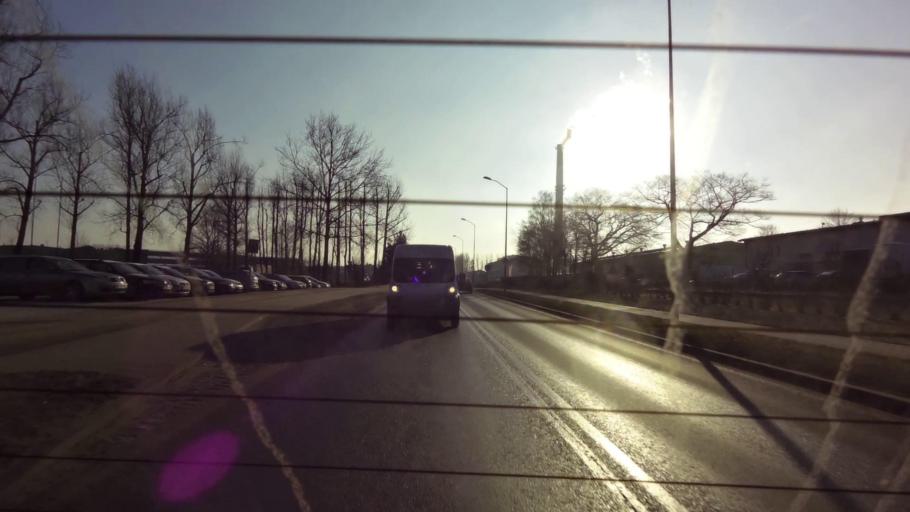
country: PL
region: West Pomeranian Voivodeship
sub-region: Koszalin
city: Koszalin
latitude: 54.1792
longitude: 16.1711
